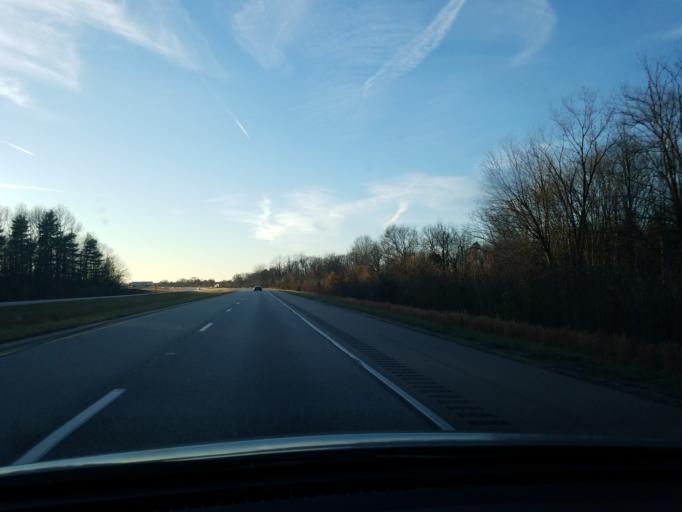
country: US
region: Indiana
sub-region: Gibson County
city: Oakland City
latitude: 38.1926
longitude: -87.3342
